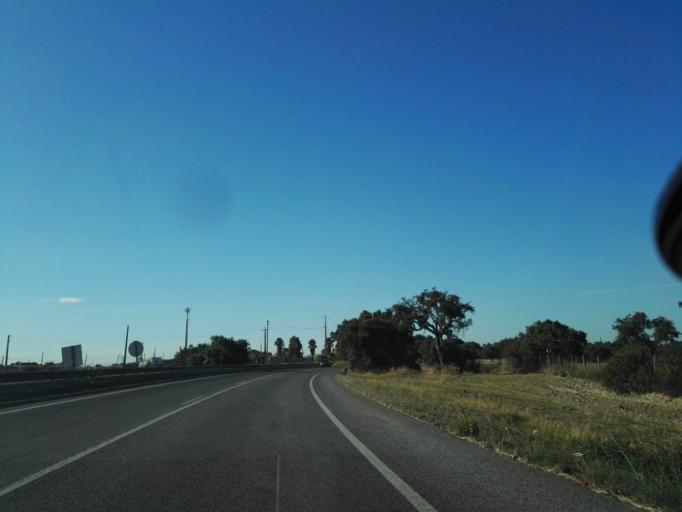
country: PT
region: Santarem
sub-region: Benavente
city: Samora Correia
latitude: 38.8969
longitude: -8.8384
